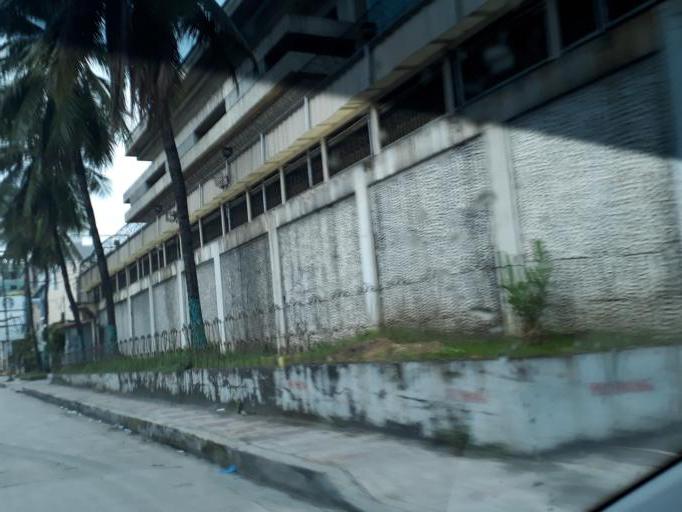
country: PH
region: Calabarzon
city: Del Monte
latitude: 14.6411
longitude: 121.0005
